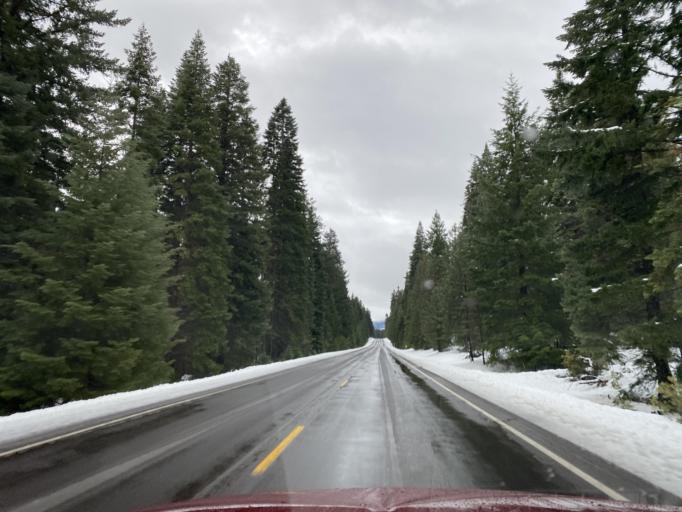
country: US
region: Oregon
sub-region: Klamath County
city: Klamath Falls
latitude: 42.5186
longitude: -122.0839
